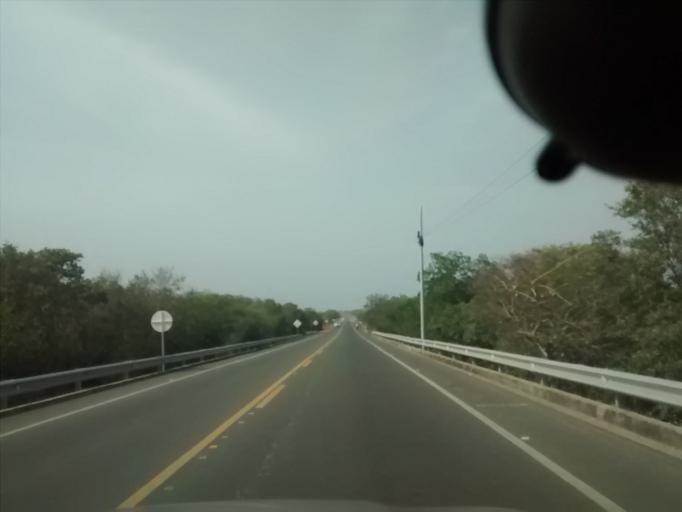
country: CO
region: Bolivar
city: Cartagena
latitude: 10.4925
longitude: -75.4814
